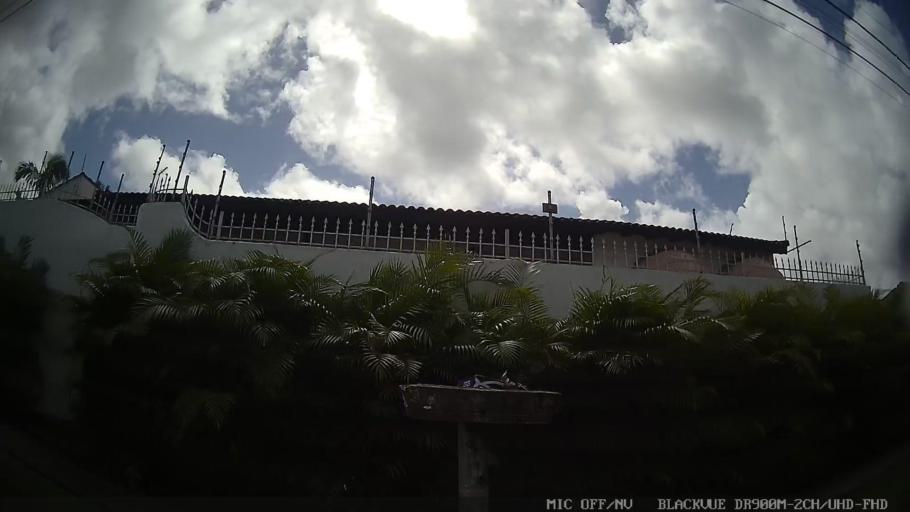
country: BR
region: Sao Paulo
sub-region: Itanhaem
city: Itanhaem
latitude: -24.2019
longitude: -46.8210
